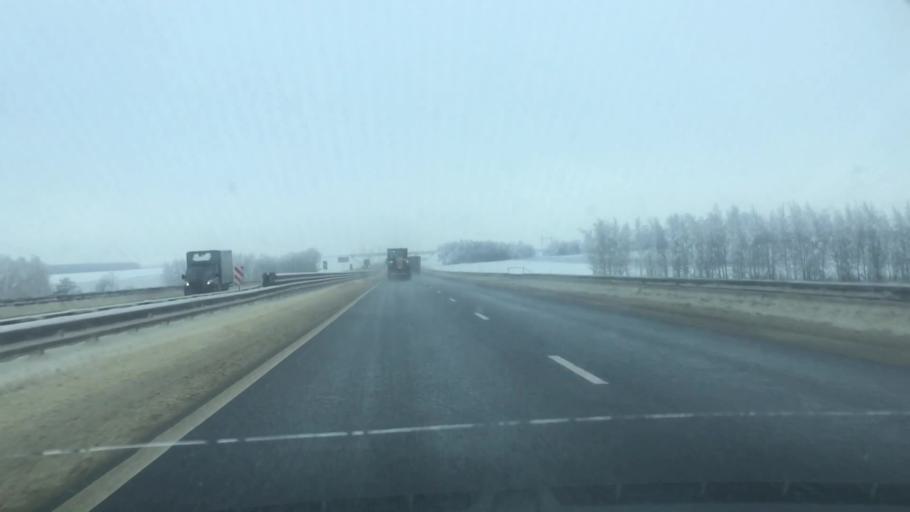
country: RU
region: Lipetsk
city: Yelets
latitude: 52.7382
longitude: 38.4859
